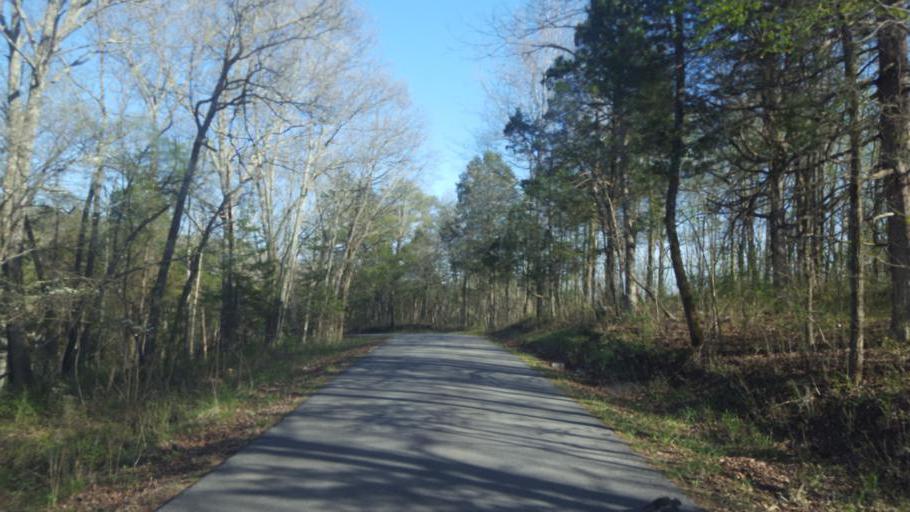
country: US
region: Kentucky
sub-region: Barren County
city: Cave City
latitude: 37.2032
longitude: -86.0212
